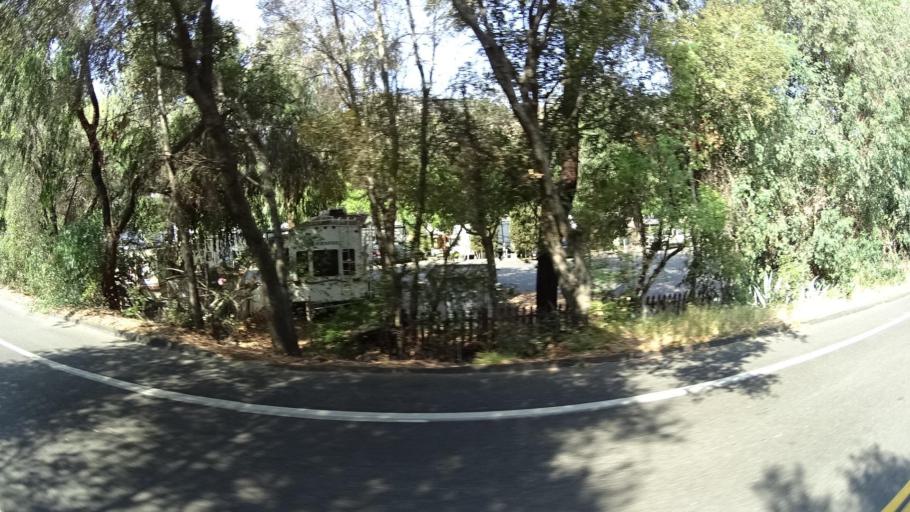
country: US
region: California
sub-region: San Diego County
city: Hidden Meadows
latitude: 33.2577
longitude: -117.1548
